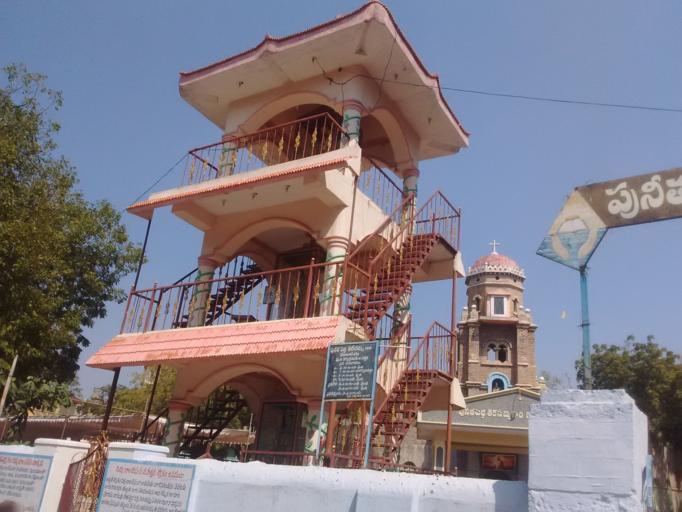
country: IN
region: Telangana
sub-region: Mahbubnagar
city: Alampur
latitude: 15.8335
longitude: 78.0423
